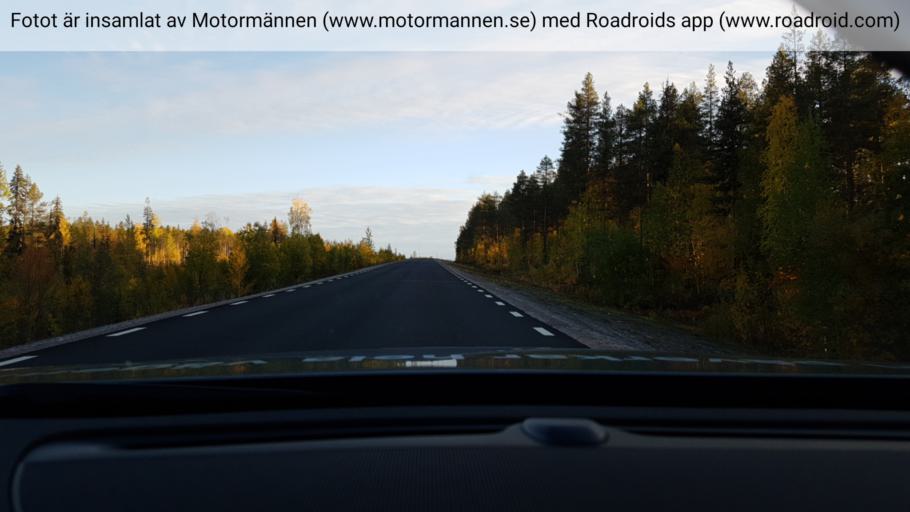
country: SE
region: Norrbotten
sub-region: Jokkmokks Kommun
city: Jokkmokk
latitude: 66.5857
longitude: 19.8025
